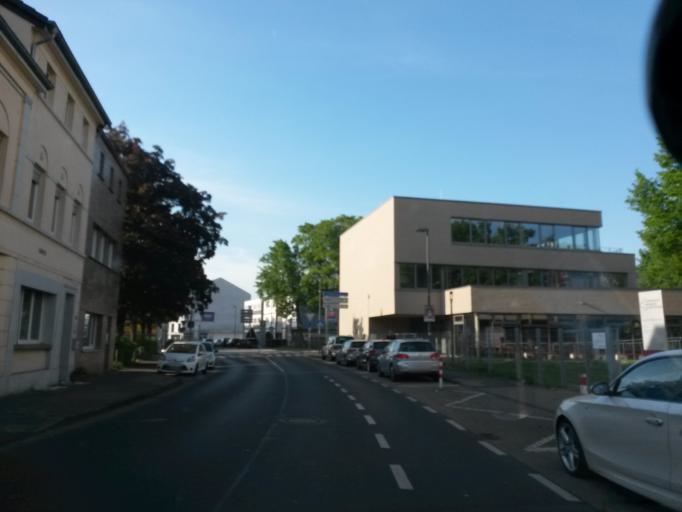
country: DE
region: North Rhine-Westphalia
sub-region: Regierungsbezirk Koln
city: Siegburg
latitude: 50.7974
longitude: 7.2028
